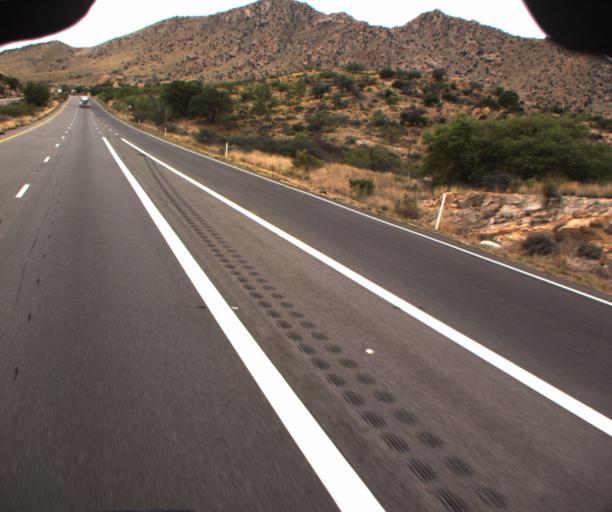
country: US
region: Arizona
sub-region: Cochise County
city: Saint David
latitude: 32.0406
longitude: -110.0961
